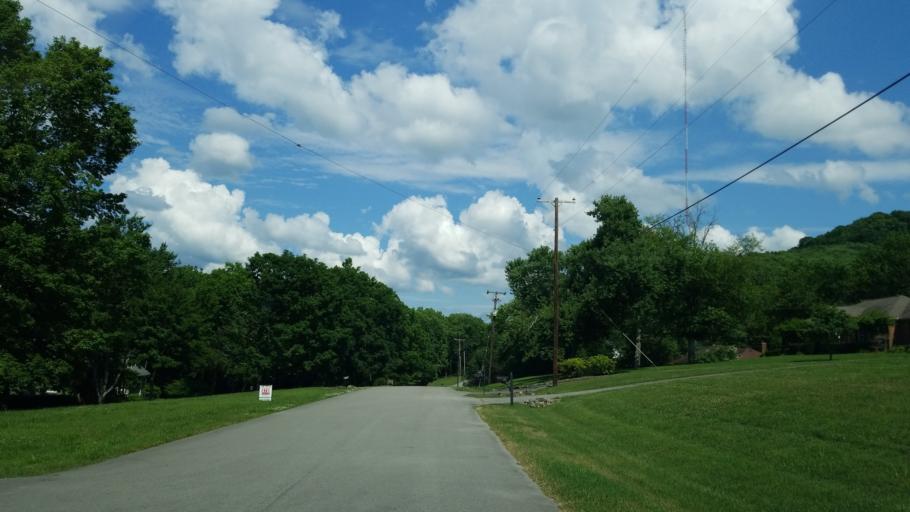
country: US
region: Tennessee
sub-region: Davidson County
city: Forest Hills
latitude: 36.0392
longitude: -86.8568
